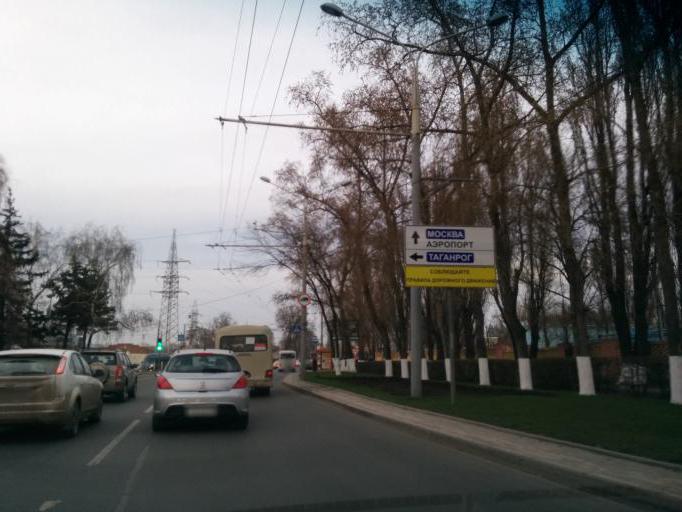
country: RU
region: Rostov
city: Rostov-na-Donu
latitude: 47.2357
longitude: 39.7390
